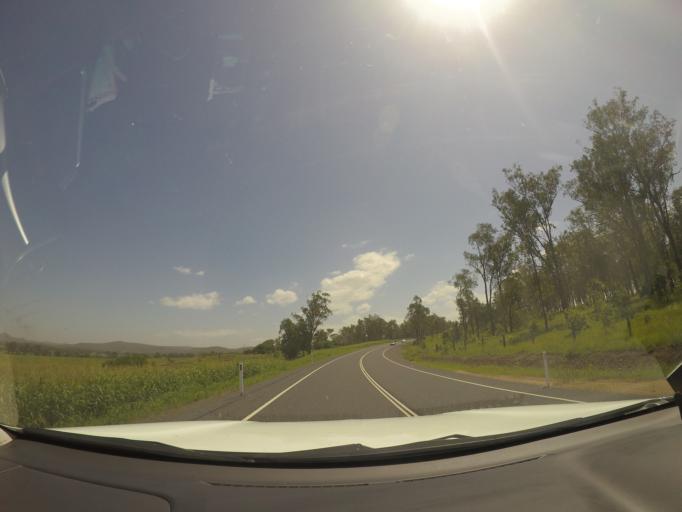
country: AU
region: Queensland
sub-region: Logan
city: Cedar Vale
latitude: -27.8604
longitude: 152.9243
